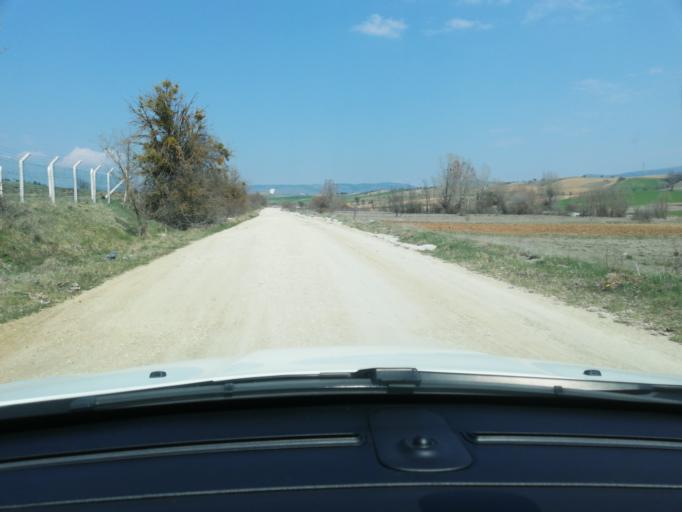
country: TR
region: Kastamonu
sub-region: Cide
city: Kastamonu
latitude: 41.4634
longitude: 33.7657
